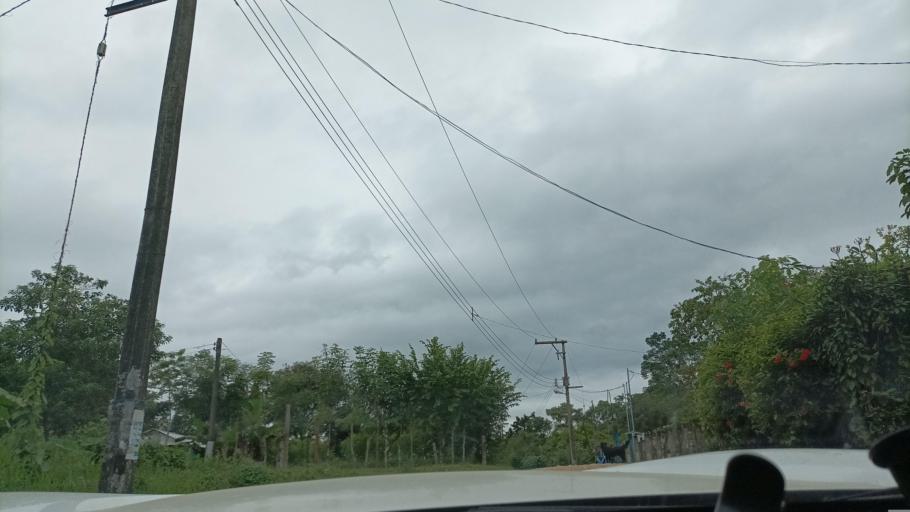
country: MX
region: Veracruz
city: Hidalgotitlan
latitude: 17.8080
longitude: -94.5373
